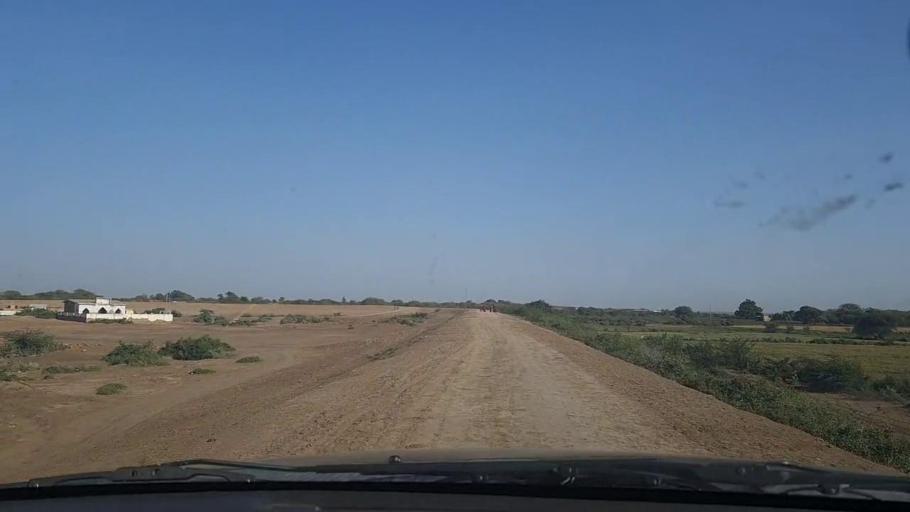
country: PK
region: Sindh
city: Chuhar Jamali
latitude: 24.3680
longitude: 67.7762
